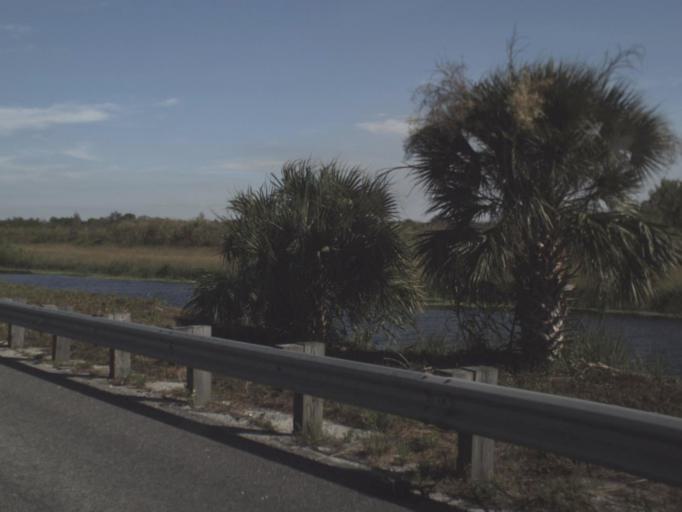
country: US
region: Florida
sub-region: Glades County
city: Moore Haven
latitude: 26.7537
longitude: -81.0440
